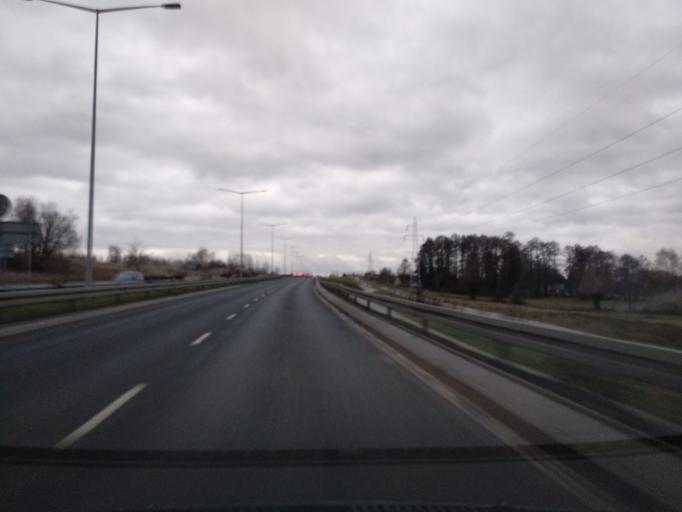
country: PL
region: Greater Poland Voivodeship
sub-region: Powiat koninski
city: Stare Miasto
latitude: 52.2018
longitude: 18.2255
